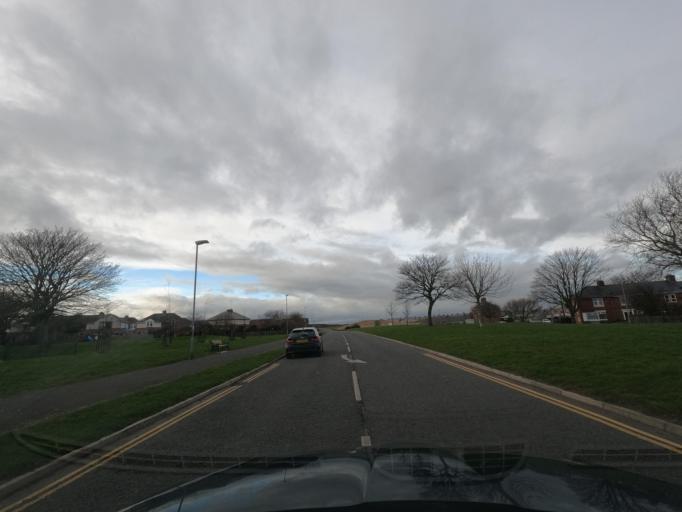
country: GB
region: England
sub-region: Northumberland
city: Newbiggin-by-the-Sea
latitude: 55.1835
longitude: -1.5171
